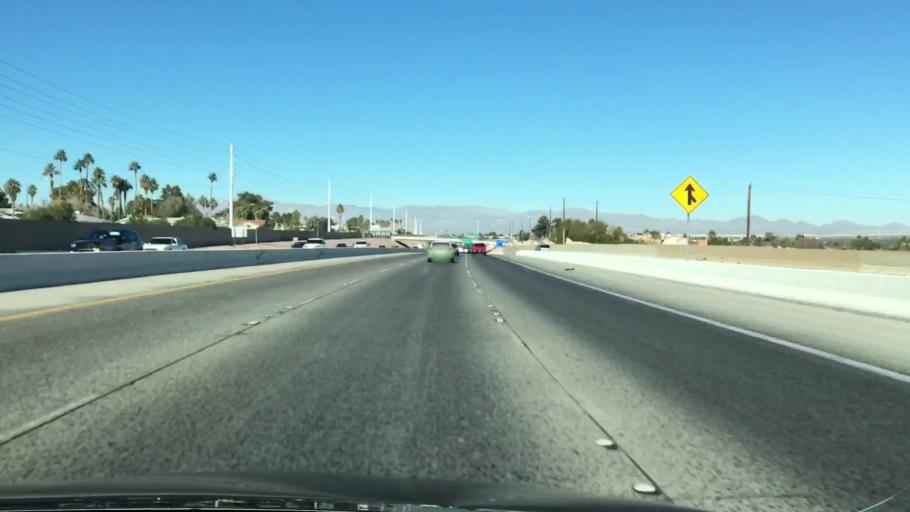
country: US
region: Nevada
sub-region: Clark County
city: Whitney
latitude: 36.1026
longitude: -115.0821
